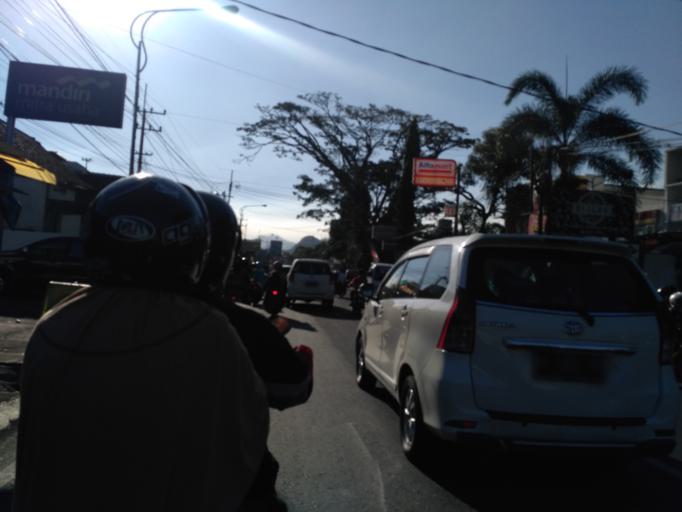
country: ID
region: East Java
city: Batu
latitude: -7.9150
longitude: 112.5864
